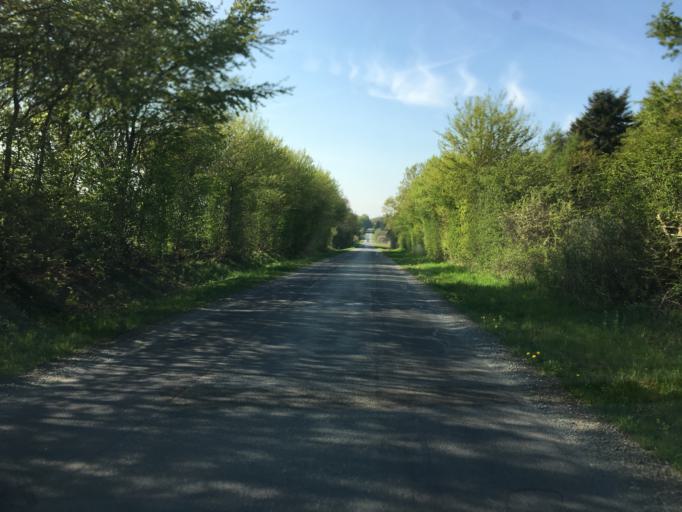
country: DK
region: South Denmark
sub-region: Haderslev Kommune
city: Vojens
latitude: 55.2346
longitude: 9.3288
